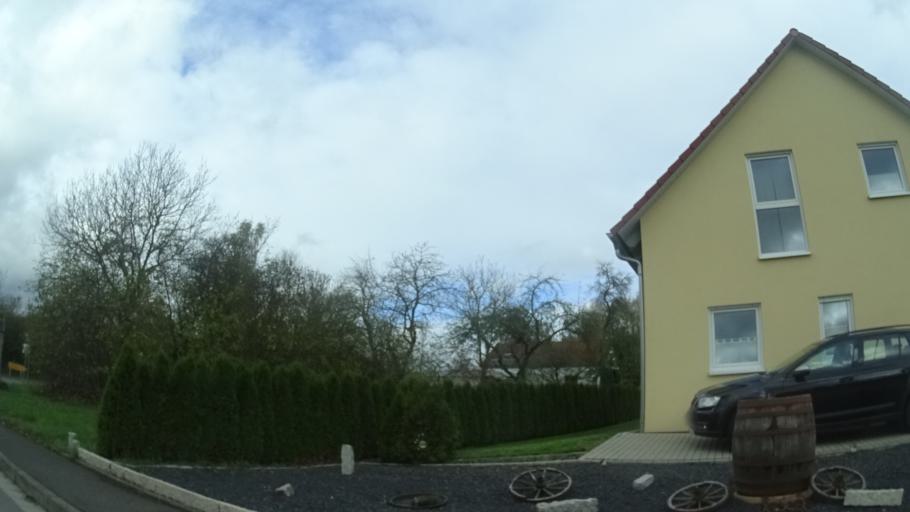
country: DE
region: Bavaria
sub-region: Regierungsbezirk Unterfranken
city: Wuelfershausen
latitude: 50.3335
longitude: 10.3425
